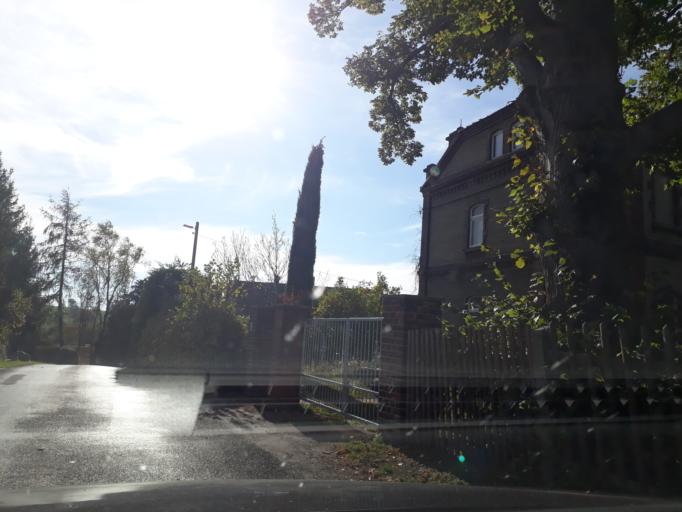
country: DE
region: Saxony
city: Niederstriegis
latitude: 51.1014
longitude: 13.1565
